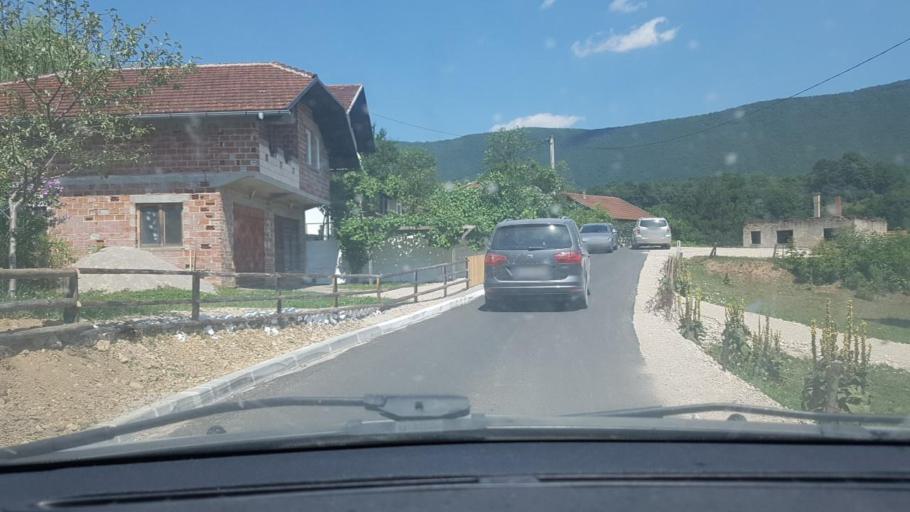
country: BA
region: Federation of Bosnia and Herzegovina
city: Orasac
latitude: 44.6229
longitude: 16.0651
